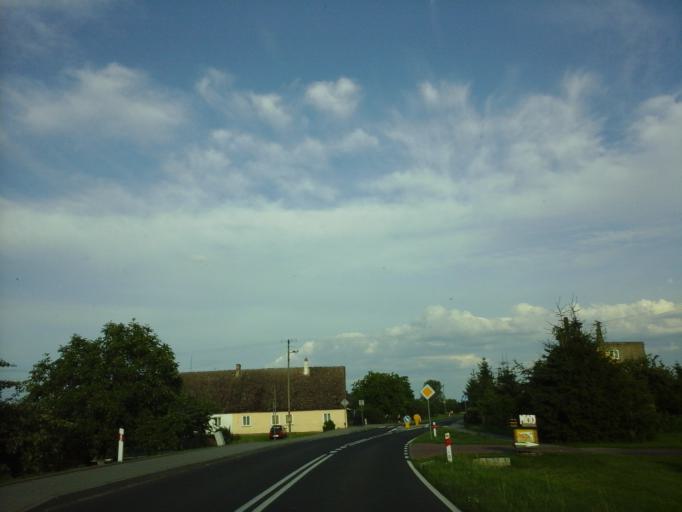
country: PL
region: West Pomeranian Voivodeship
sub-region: Powiat kamienski
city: Kamien Pomorski
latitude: 53.9263
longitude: 14.8372
